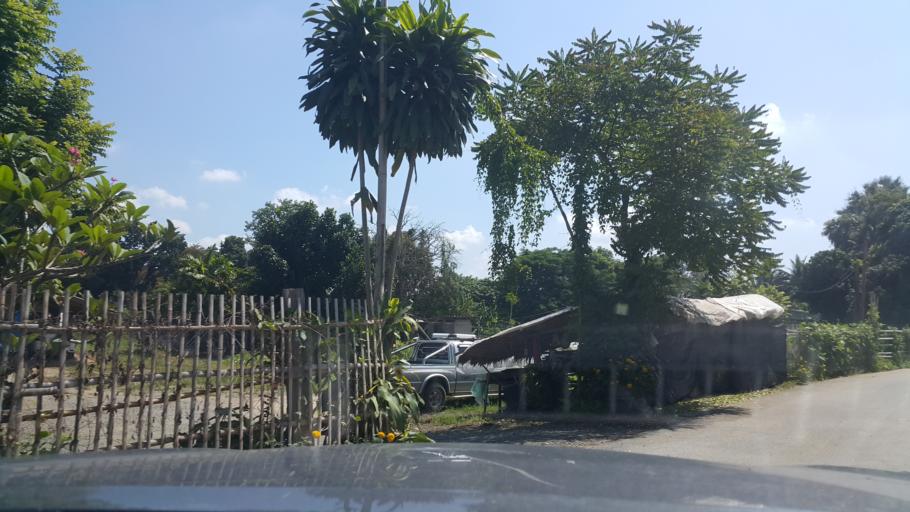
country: TH
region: Chiang Mai
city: Chiang Mai
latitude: 18.8469
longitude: 98.9840
